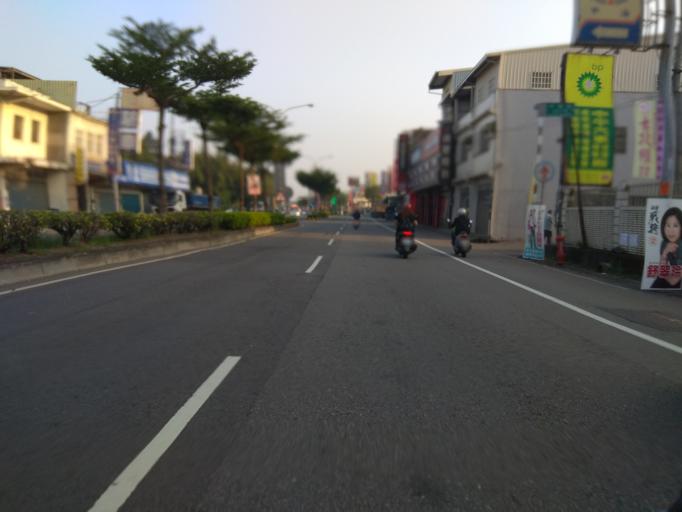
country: TW
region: Taiwan
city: Daxi
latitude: 24.9337
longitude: 121.2152
